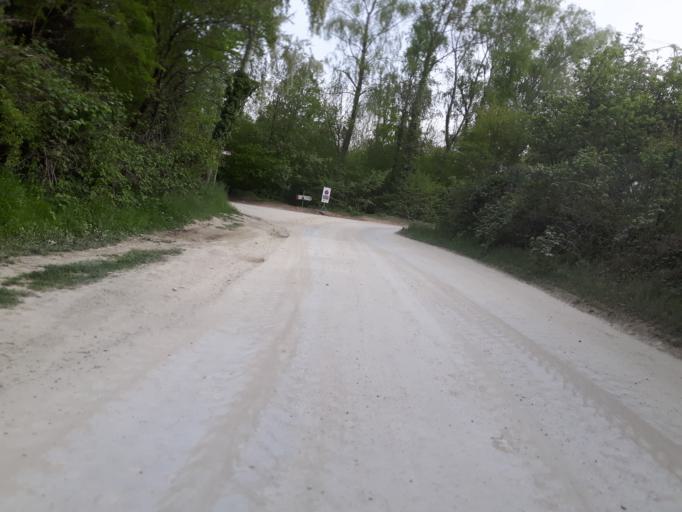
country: CH
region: Vaud
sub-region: Jura-Nord vaudois District
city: Grandson
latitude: 46.8247
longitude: 6.6792
